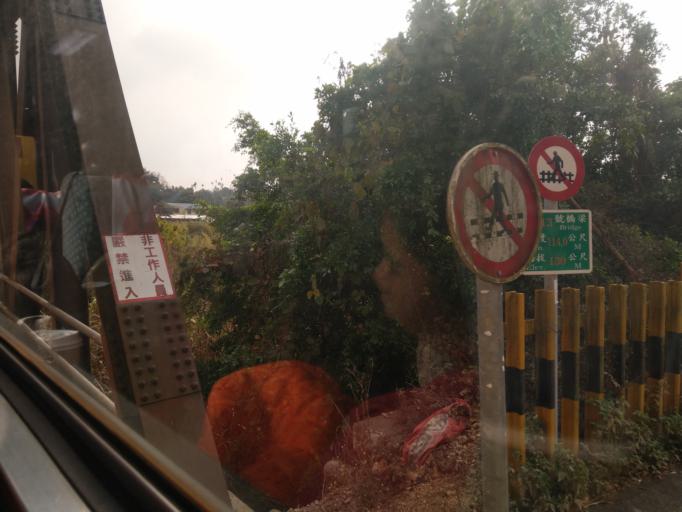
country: TW
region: Taiwan
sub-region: Chiayi
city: Jiayi Shi
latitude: 23.5278
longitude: 120.5548
